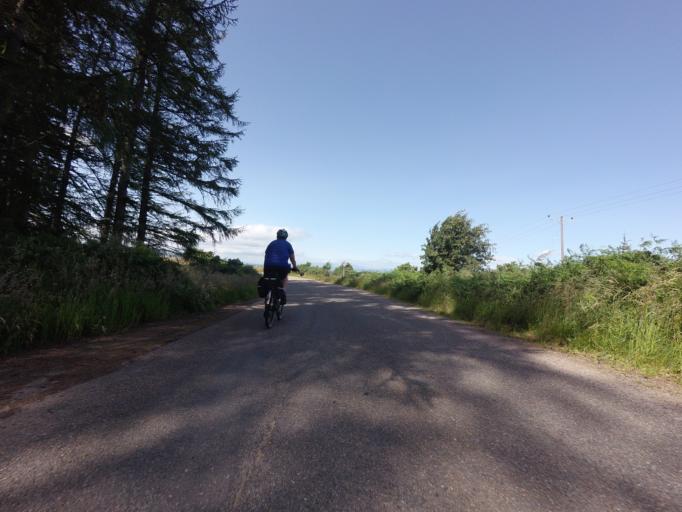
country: GB
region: Scotland
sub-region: Highland
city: Nairn
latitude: 57.5007
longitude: -3.9736
